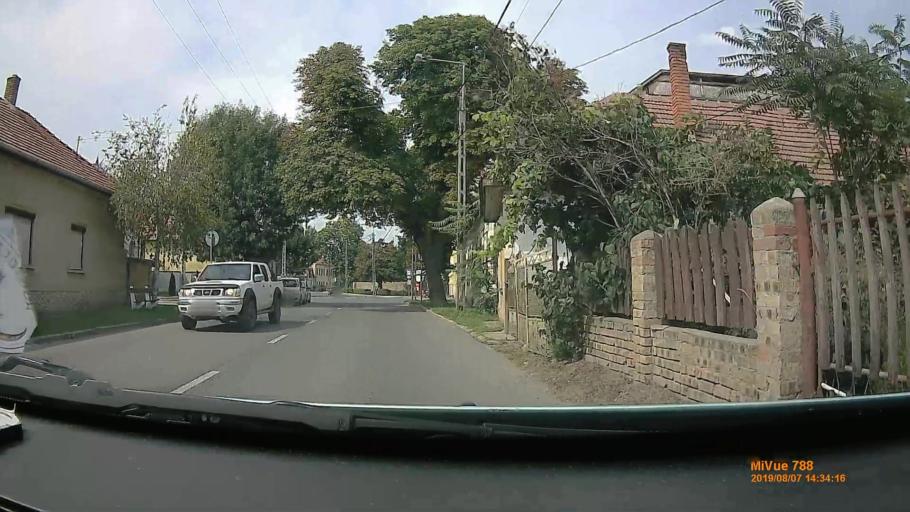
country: HU
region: Borsod-Abauj-Zemplen
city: Szikszo
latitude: 48.2001
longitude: 20.9272
